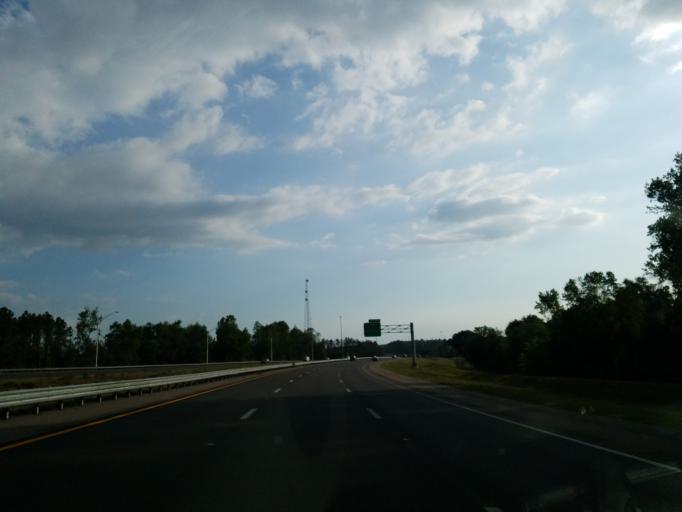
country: US
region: Florida
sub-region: Pasco County
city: San Antonio
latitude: 28.4242
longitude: -82.2825
